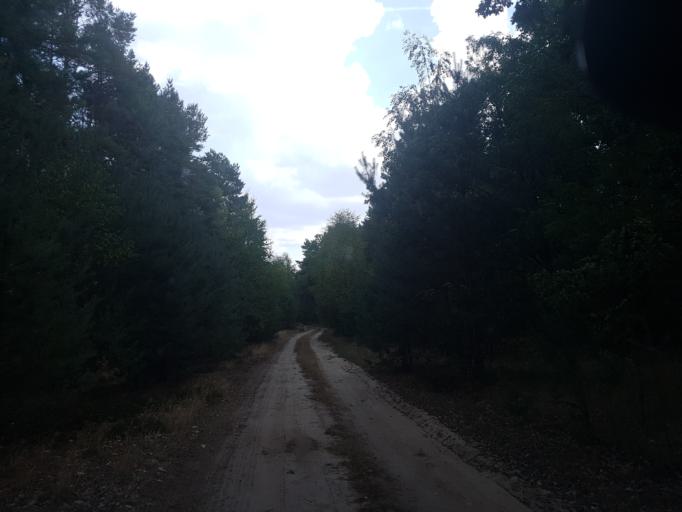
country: DE
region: Brandenburg
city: Treuenbrietzen
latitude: 52.0444
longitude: 12.8576
